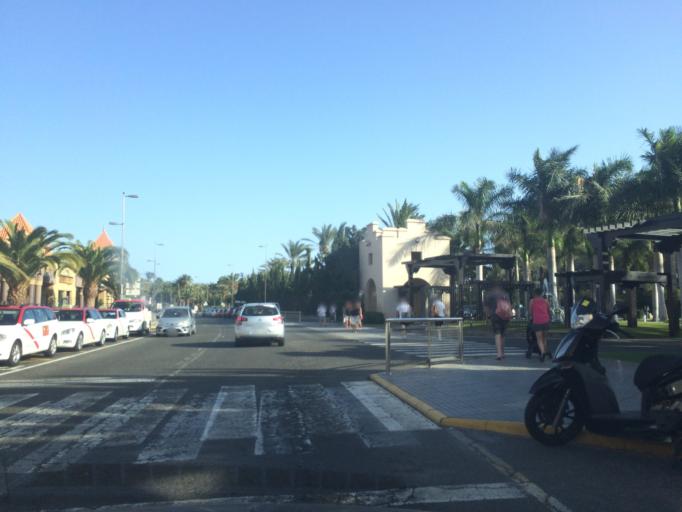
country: ES
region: Canary Islands
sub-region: Provincia de Las Palmas
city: Maspalomas
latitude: 27.7392
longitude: -15.6001
